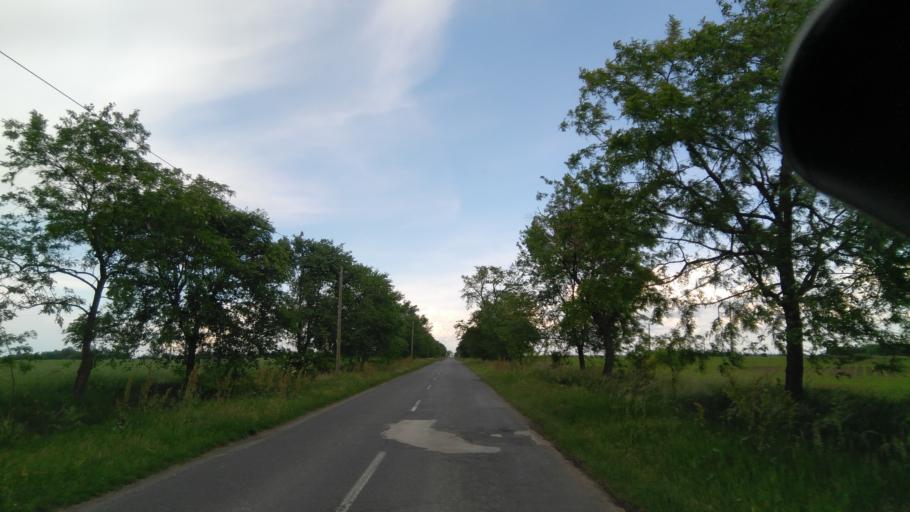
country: HU
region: Bekes
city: Dombegyhaz
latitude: 46.3512
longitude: 21.1589
